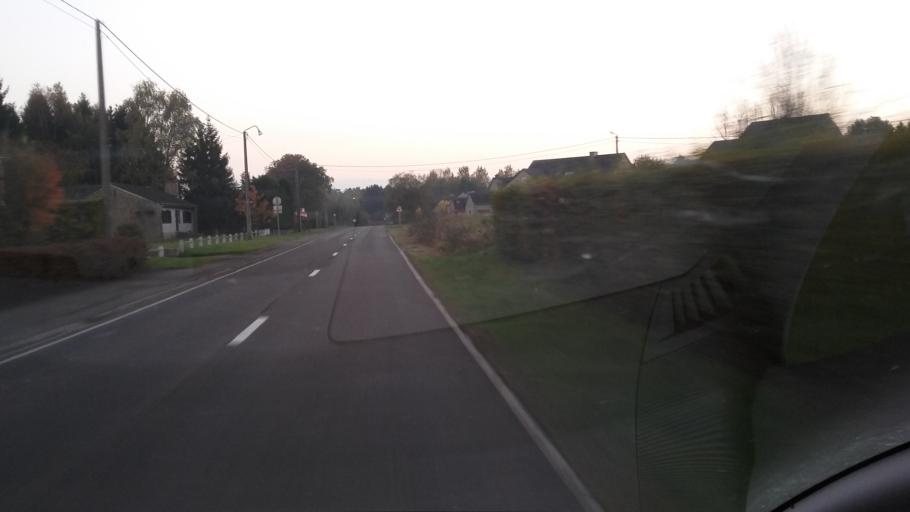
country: BE
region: Wallonia
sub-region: Province du Luxembourg
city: Etalle
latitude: 49.6677
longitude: 5.5983
